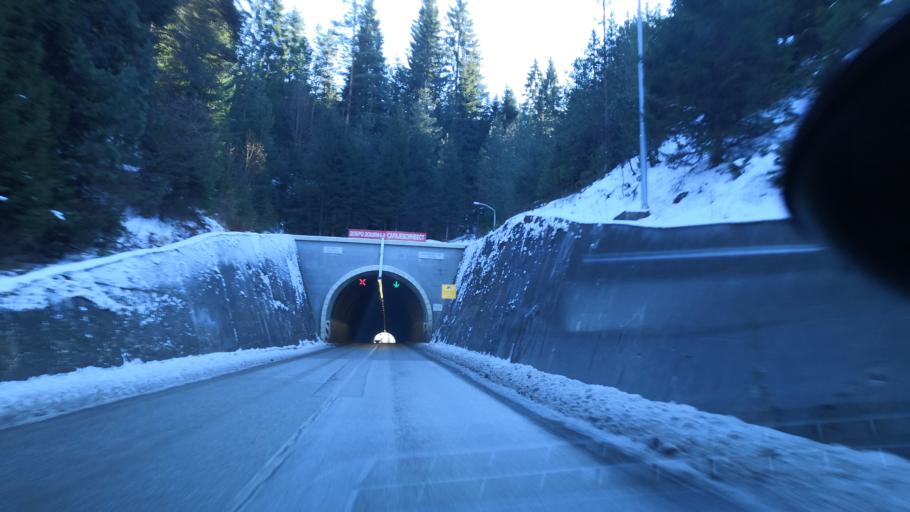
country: BA
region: Republika Srpska
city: Pale
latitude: 43.8306
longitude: 18.5581
